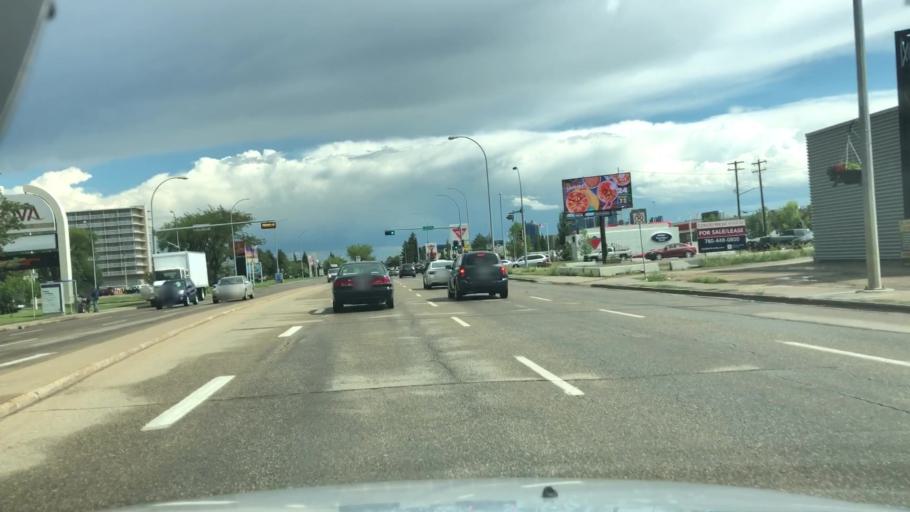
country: CA
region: Alberta
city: Edmonton
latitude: 53.5689
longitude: -113.5276
